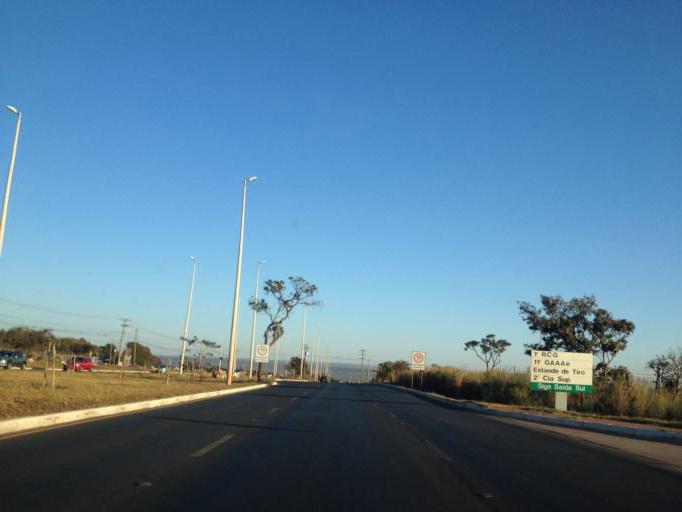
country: BR
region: Federal District
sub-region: Brasilia
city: Brasilia
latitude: -15.7616
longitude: -47.9203
